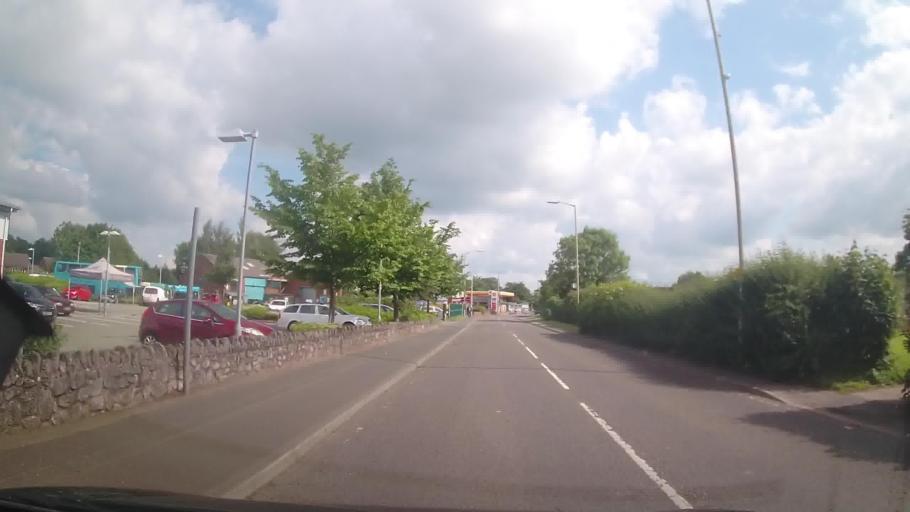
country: GB
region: England
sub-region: Shropshire
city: Oswestry
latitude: 52.8556
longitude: -3.0495
